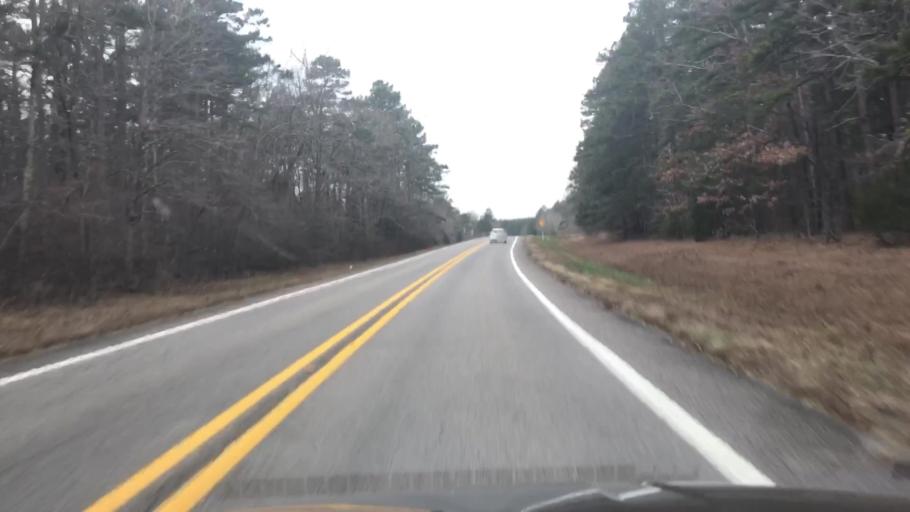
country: US
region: Arkansas
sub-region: Montgomery County
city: Mount Ida
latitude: 34.6851
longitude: -93.8535
